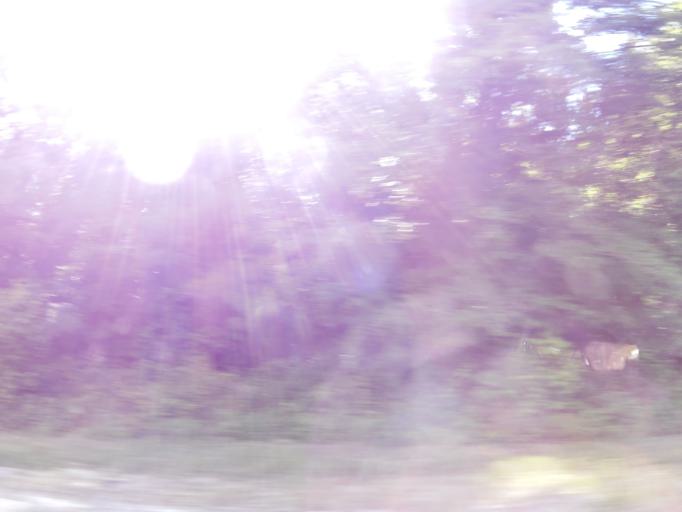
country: US
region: South Carolina
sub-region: Allendale County
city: Fairfax
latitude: 32.9981
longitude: -81.2208
